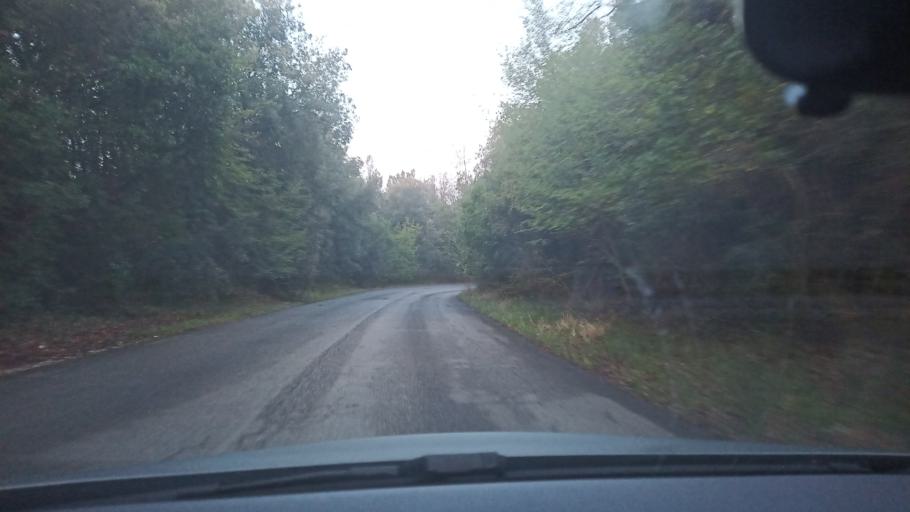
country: IT
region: Latium
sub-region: Provincia di Rieti
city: Montasola
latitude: 42.3650
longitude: 12.6652
